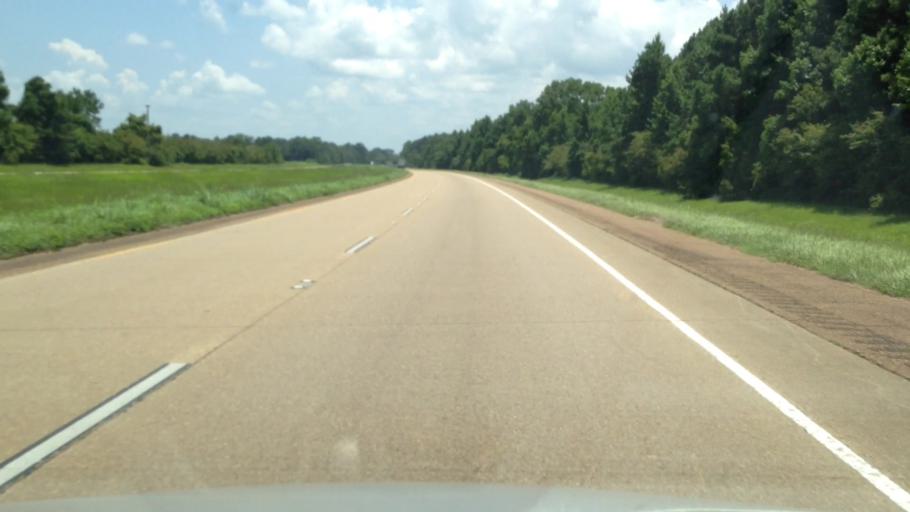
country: US
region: Louisiana
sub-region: Rapides Parish
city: Woodworth
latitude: 31.1400
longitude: -92.4510
